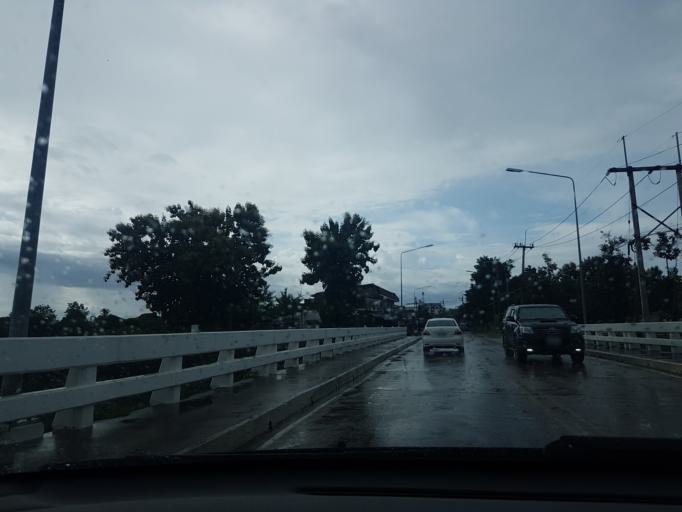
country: TH
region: Lampang
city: Lampang
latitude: 18.2911
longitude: 99.4735
